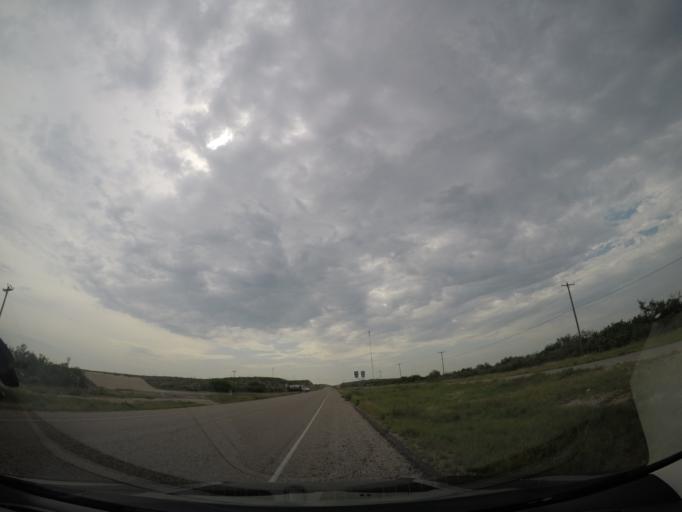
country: US
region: Texas
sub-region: Val Verde County
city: Cienegas Terrace
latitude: 29.6965
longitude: -101.1914
